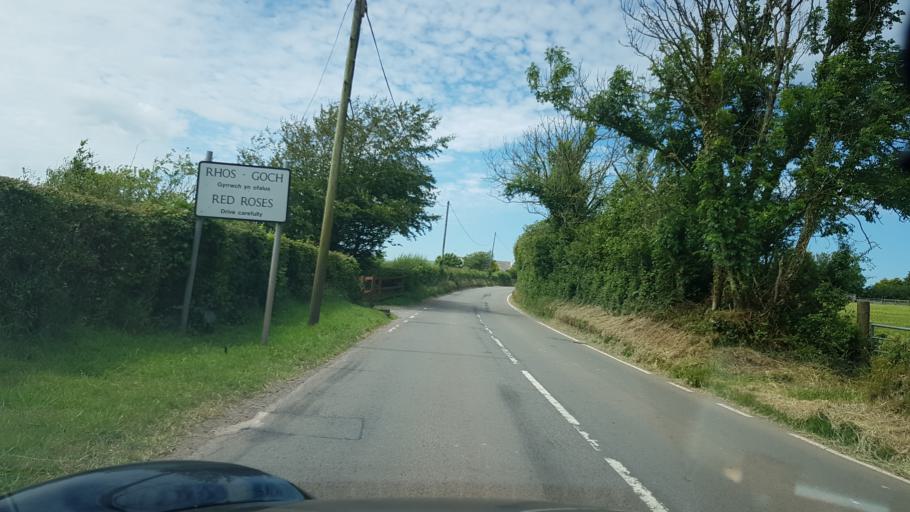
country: GB
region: Wales
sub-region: Carmarthenshire
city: Whitland
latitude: 51.7724
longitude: -4.5975
